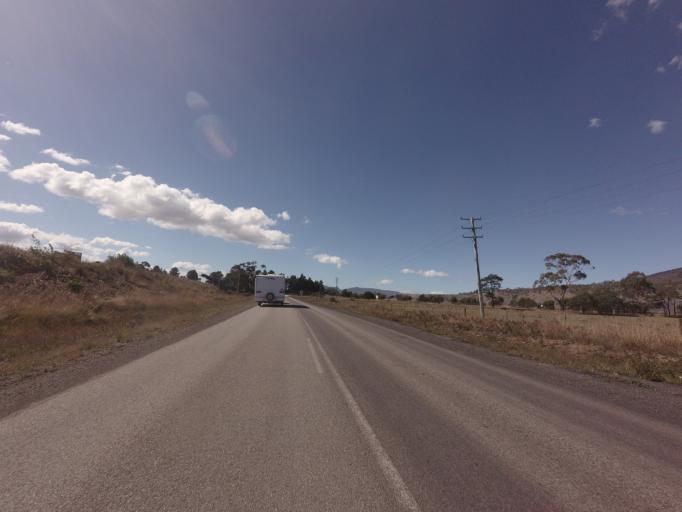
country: AU
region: Tasmania
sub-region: Break O'Day
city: St Helens
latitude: -41.6321
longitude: 147.9849
